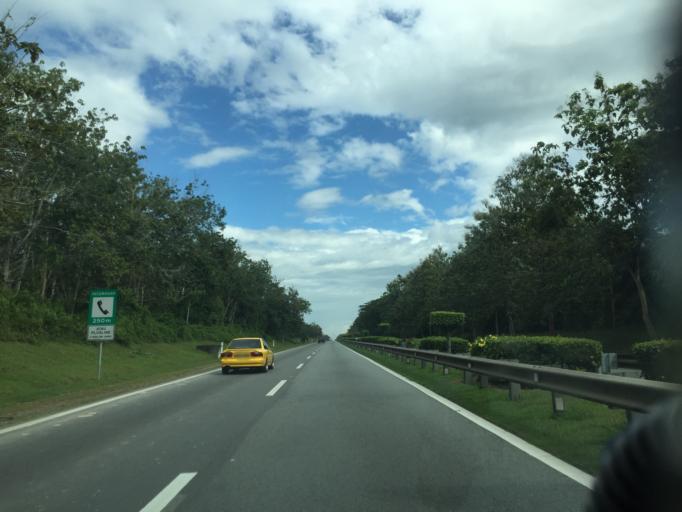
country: MY
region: Kedah
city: Jitra
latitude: 6.3716
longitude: 100.4236
